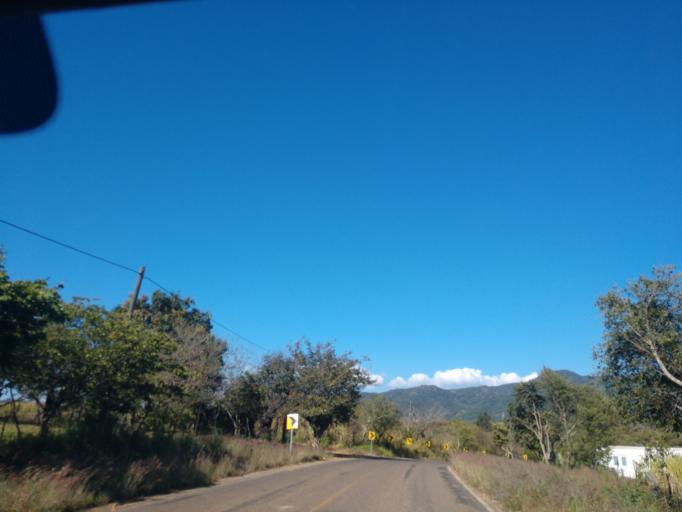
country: MX
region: Nayarit
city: Compostela
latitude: 21.2709
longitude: -104.8912
